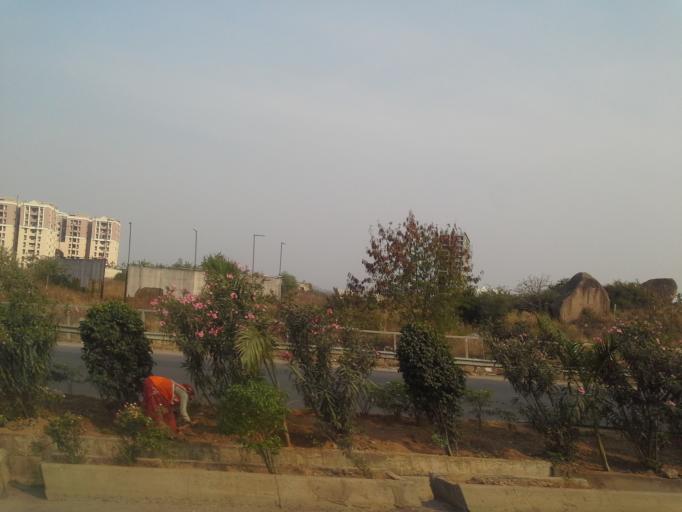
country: IN
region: Telangana
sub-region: Rangareddi
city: Kukatpalli
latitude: 17.4315
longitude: 78.3594
